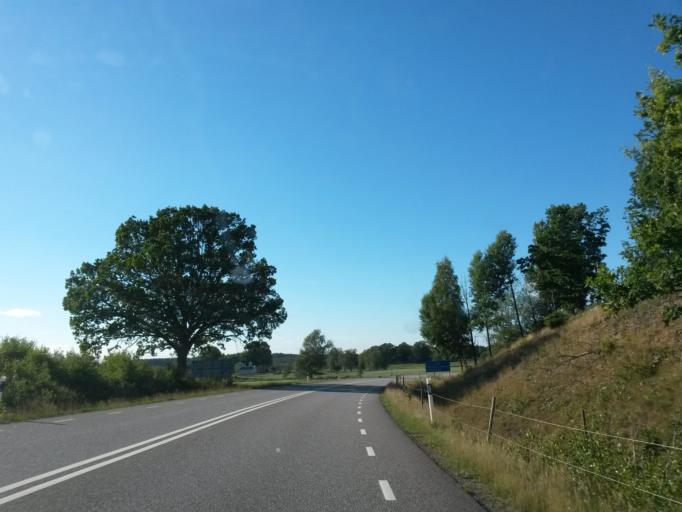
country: SE
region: Vaestra Goetaland
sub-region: Vargarda Kommun
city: Vargarda
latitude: 57.9930
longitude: 12.8100
